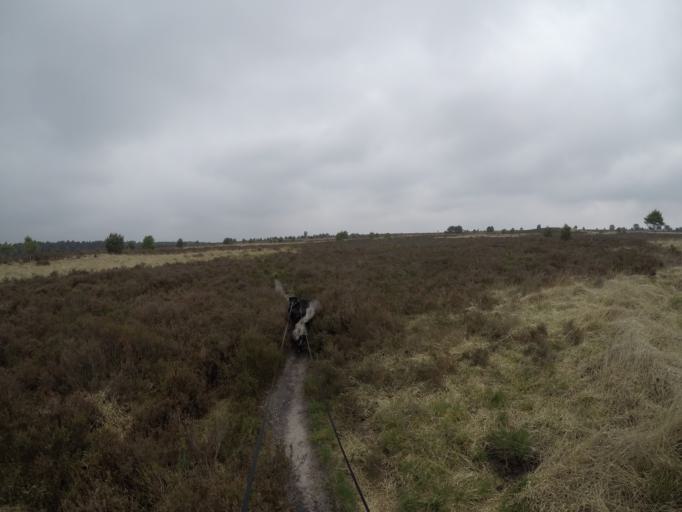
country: NL
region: Gelderland
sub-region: Gemeente Rozendaal
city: Rozendaal
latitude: 52.0303
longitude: 5.9724
